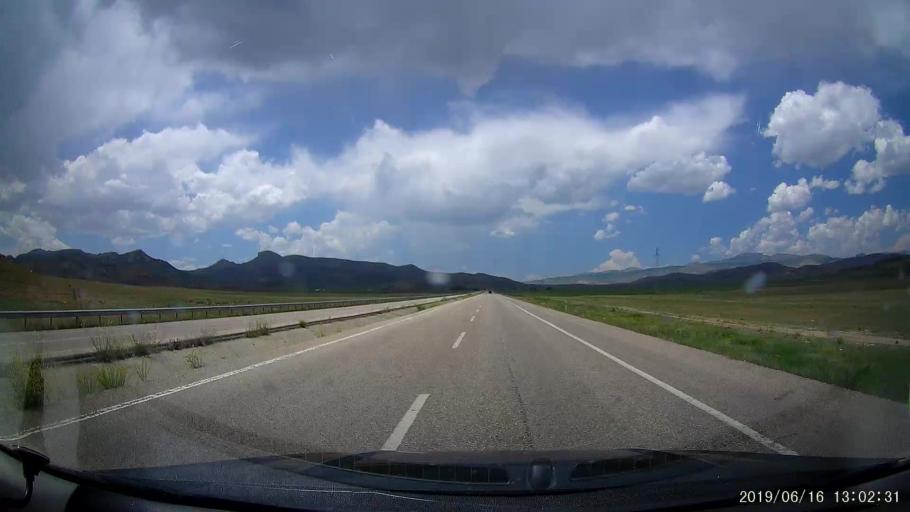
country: TR
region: Agri
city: Sulucem
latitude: 39.5751
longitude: 43.8142
